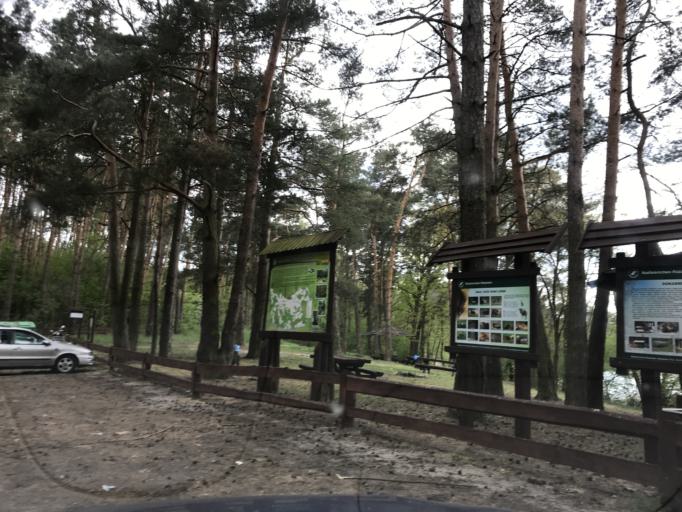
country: PL
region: West Pomeranian Voivodeship
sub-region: Powiat mysliborski
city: Mysliborz
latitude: 52.8610
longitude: 14.8876
